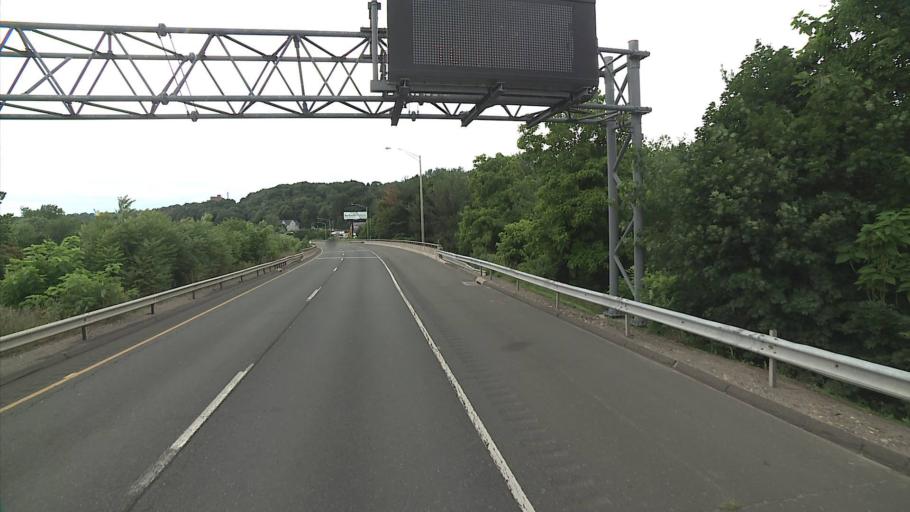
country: US
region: Connecticut
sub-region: New Haven County
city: Waterbury
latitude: 41.5680
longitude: -73.0576
